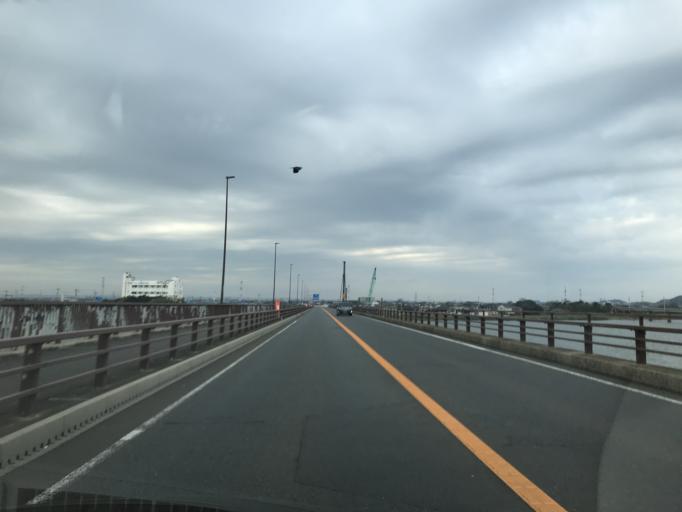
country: JP
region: Ibaraki
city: Kashima-shi
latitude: 35.9605
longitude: 140.6041
